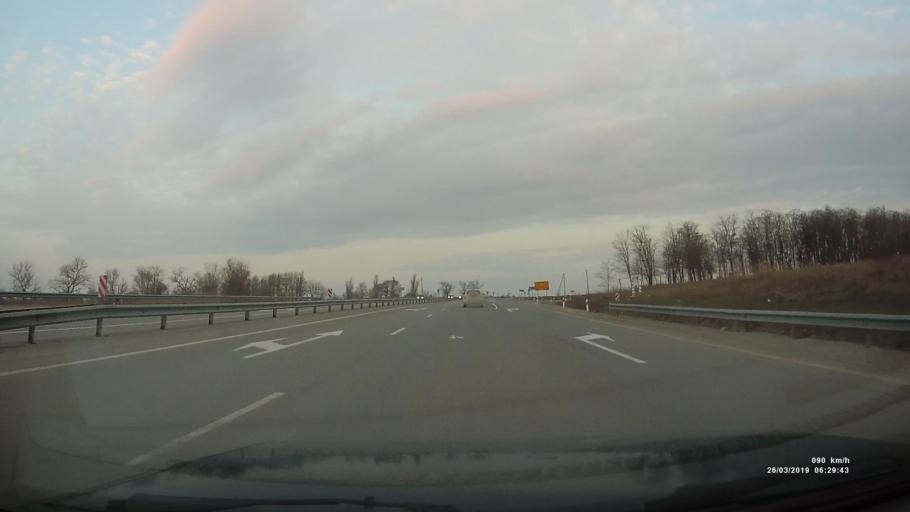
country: RU
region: Rostov
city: Kalinin
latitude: 47.2669
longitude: 39.5669
